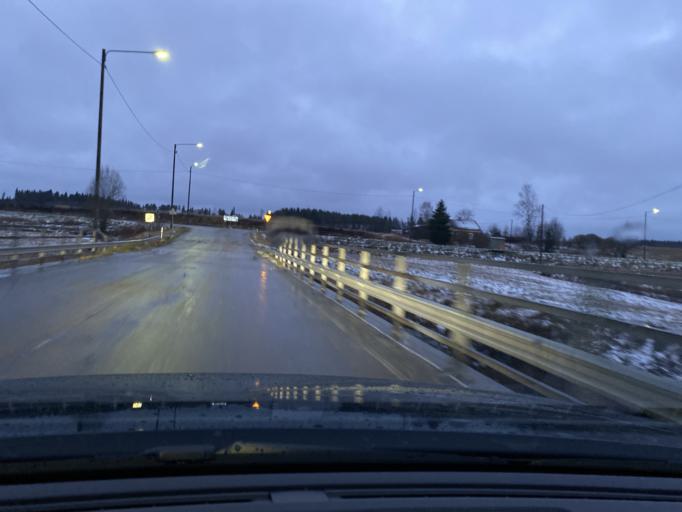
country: FI
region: Pirkanmaa
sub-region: Lounais-Pirkanmaa
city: Punkalaidun
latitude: 61.1207
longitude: 23.0512
